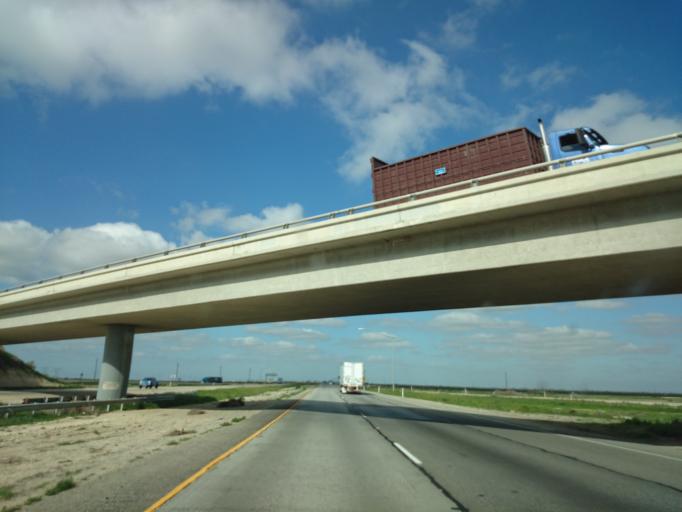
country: US
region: California
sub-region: Kern County
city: Rosedale
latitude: 35.2670
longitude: -119.2242
